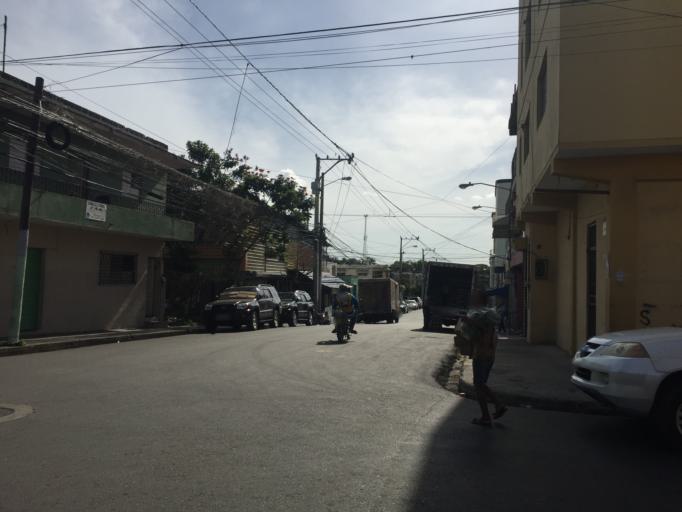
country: DO
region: Santiago
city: Santiago de los Caballeros
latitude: 19.4538
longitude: -70.7116
